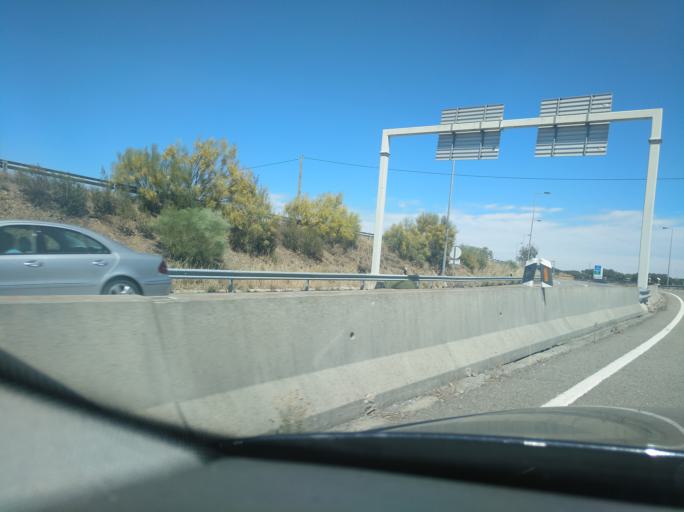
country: PT
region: Beja
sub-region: Ourique
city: Ourique
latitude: 37.6657
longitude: -8.2178
